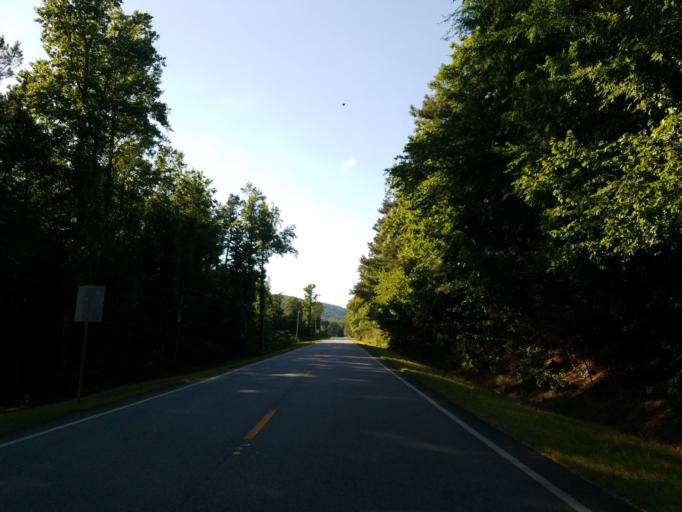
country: US
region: Georgia
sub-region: Gordon County
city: Calhoun
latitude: 34.6163
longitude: -85.0518
